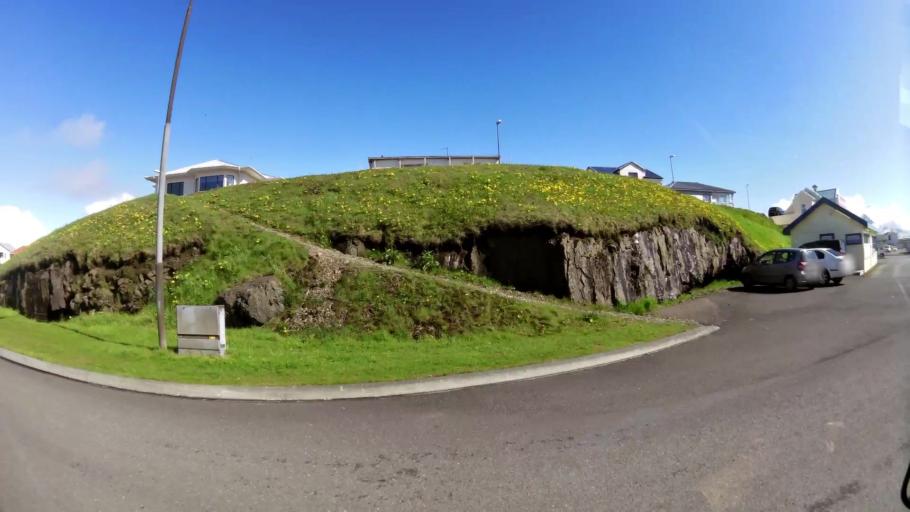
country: IS
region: East
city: Hoefn
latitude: 64.2497
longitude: -15.2077
